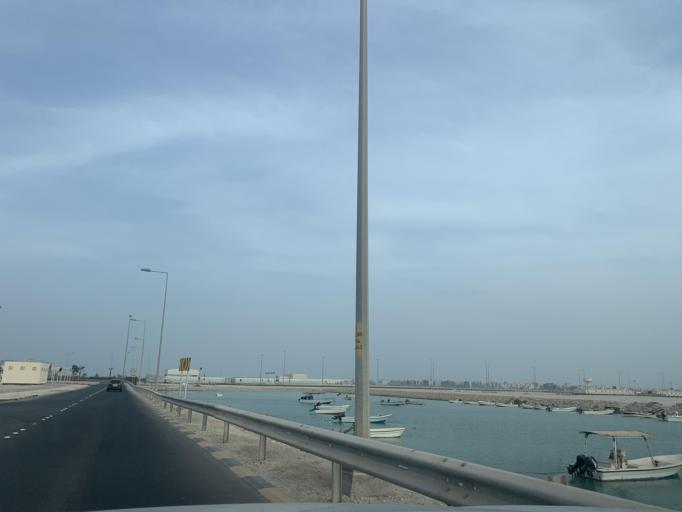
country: BH
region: Muharraq
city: Al Muharraq
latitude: 26.2960
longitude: 50.6394
